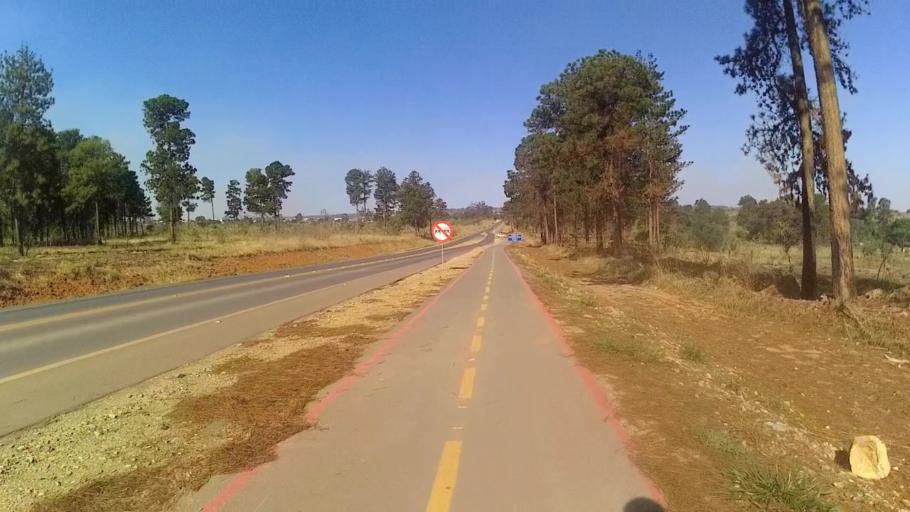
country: BR
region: Federal District
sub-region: Brasilia
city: Brasilia
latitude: -15.6778
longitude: -48.2074
